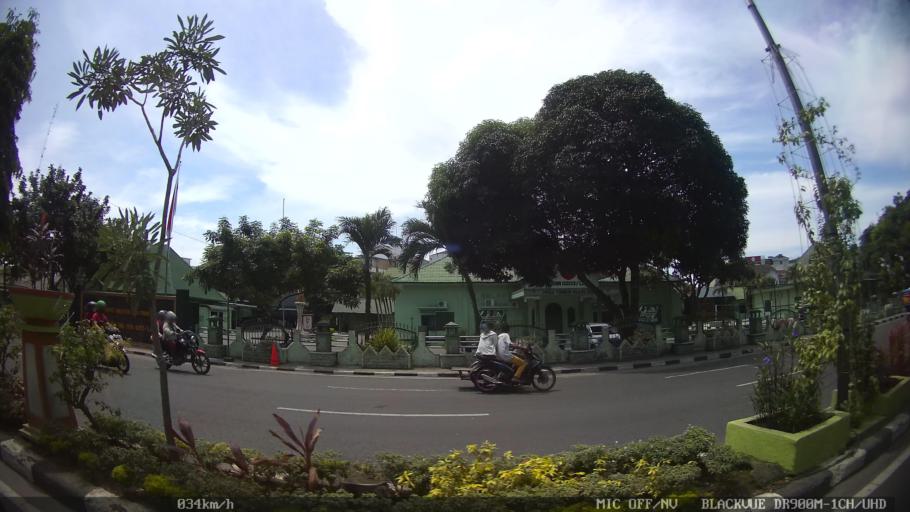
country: ID
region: North Sumatra
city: Binjai
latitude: 3.6023
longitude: 98.4811
